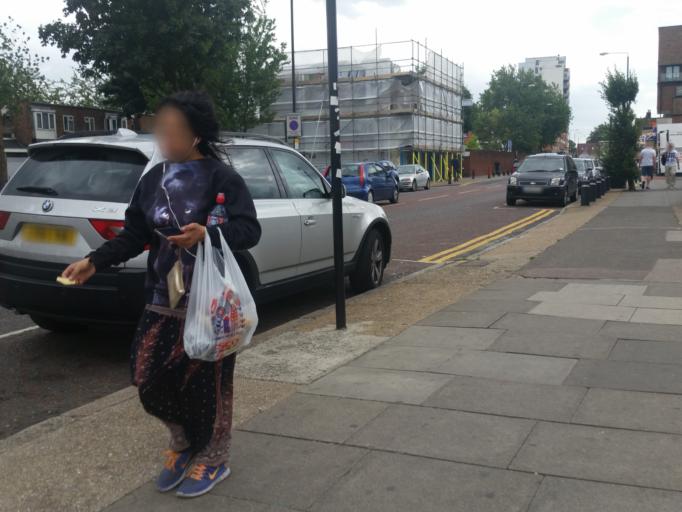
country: GB
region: England
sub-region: Greater London
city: Poplar
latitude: 51.5489
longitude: 0.0051
